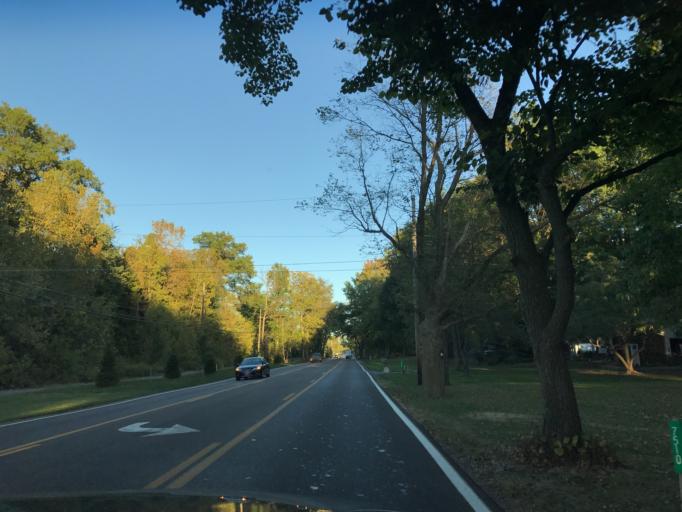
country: US
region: Ohio
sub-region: Franklin County
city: Westerville
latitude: 40.1455
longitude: -82.8954
